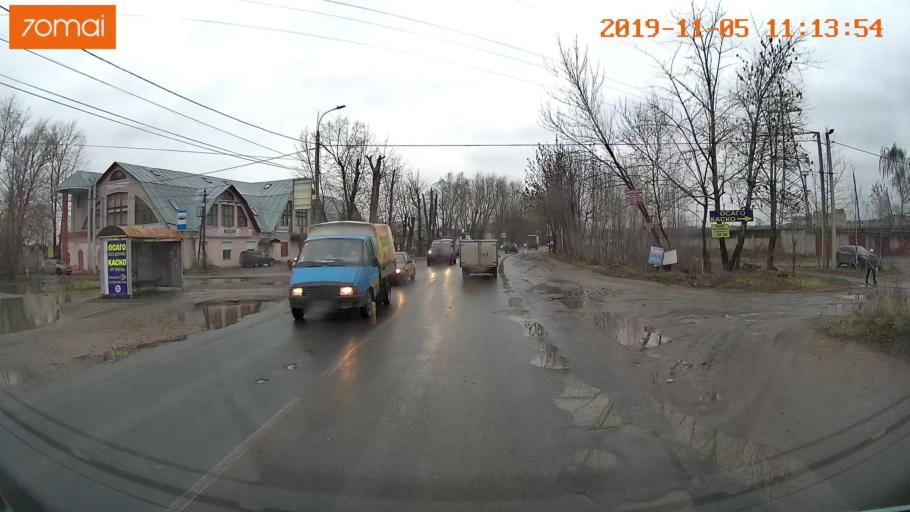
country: RU
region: Ivanovo
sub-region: Gorod Ivanovo
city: Ivanovo
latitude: 56.9677
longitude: 40.9523
